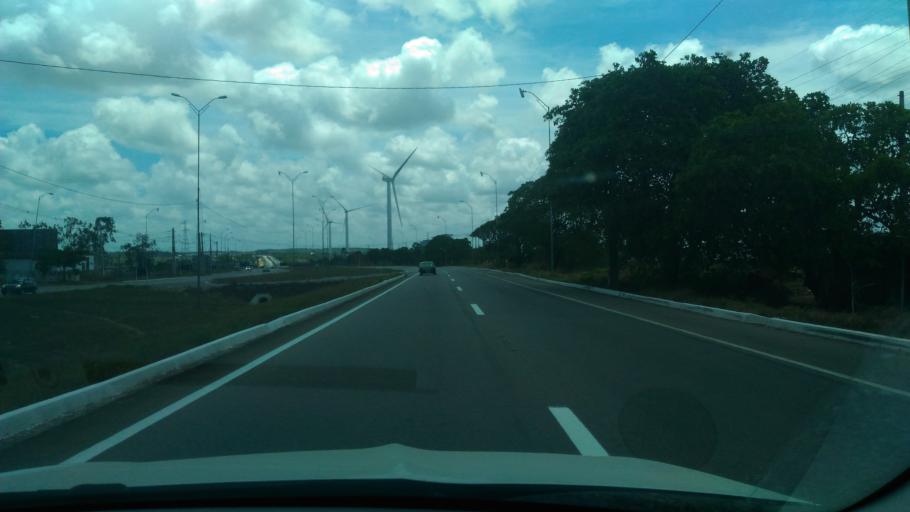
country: BR
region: Paraiba
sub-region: Conde
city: Conde
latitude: -7.2569
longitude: -34.9352
